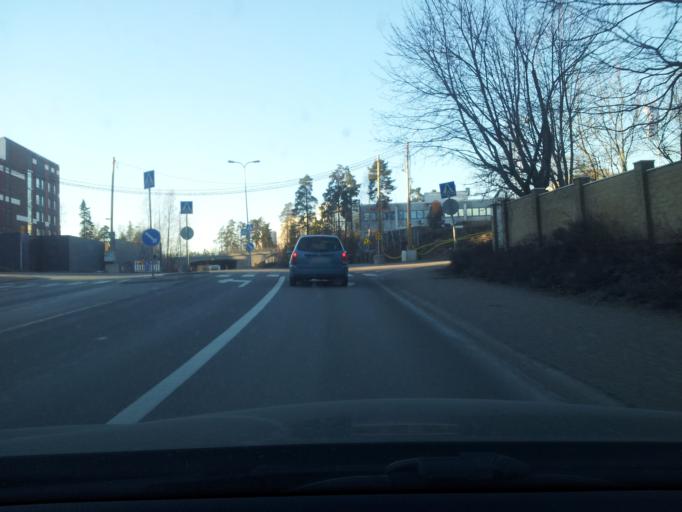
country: FI
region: Uusimaa
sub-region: Helsinki
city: Koukkuniemi
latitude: 60.1601
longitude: 24.7256
